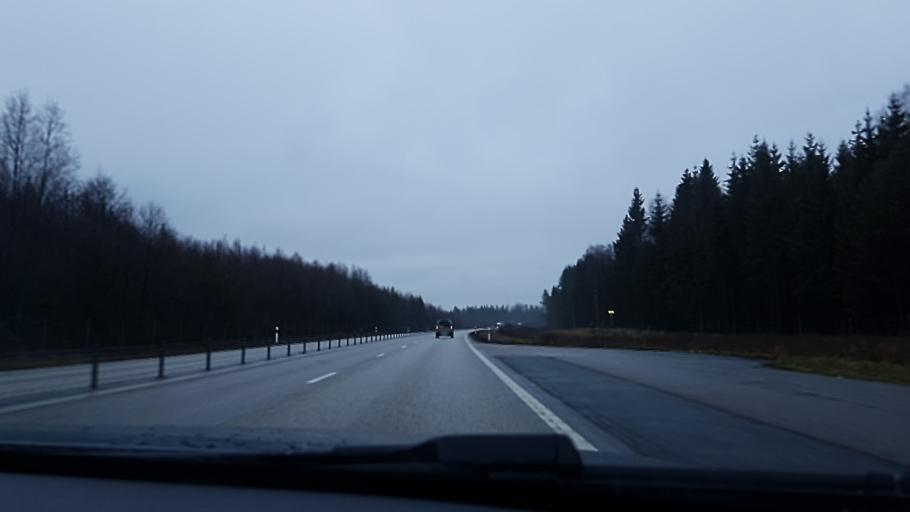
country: SE
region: Kronoberg
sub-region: Ljungby Kommun
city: Lagan
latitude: 57.0081
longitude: 14.0382
